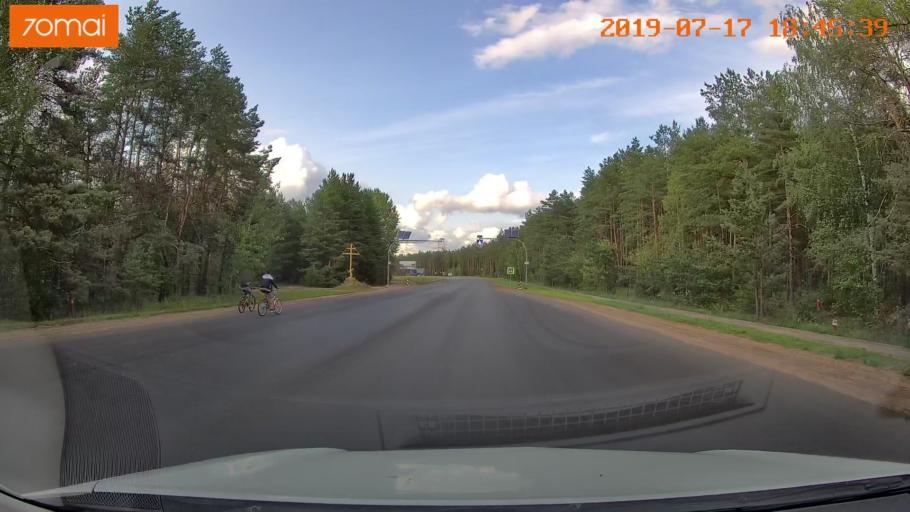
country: BY
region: Mogilev
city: Asipovichy
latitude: 53.3266
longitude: 28.6572
